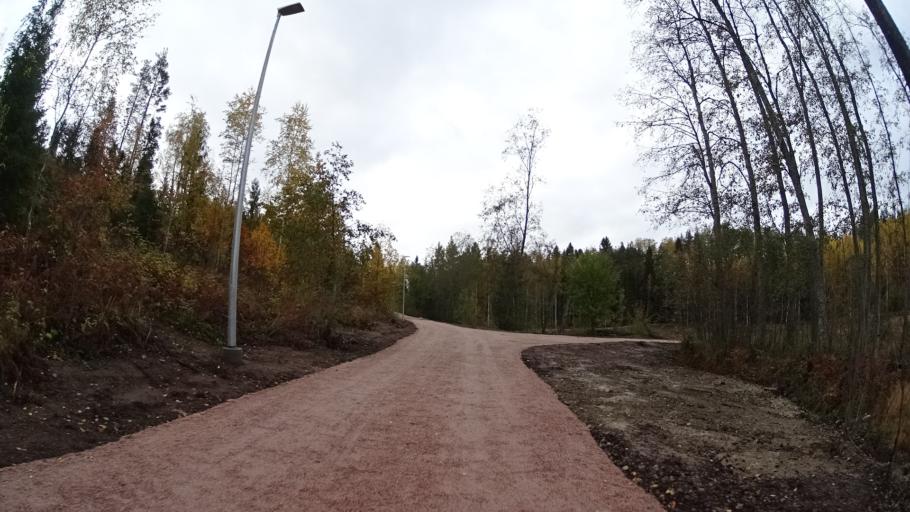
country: FI
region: Uusimaa
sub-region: Helsinki
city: Espoo
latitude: 60.2293
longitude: 24.6442
